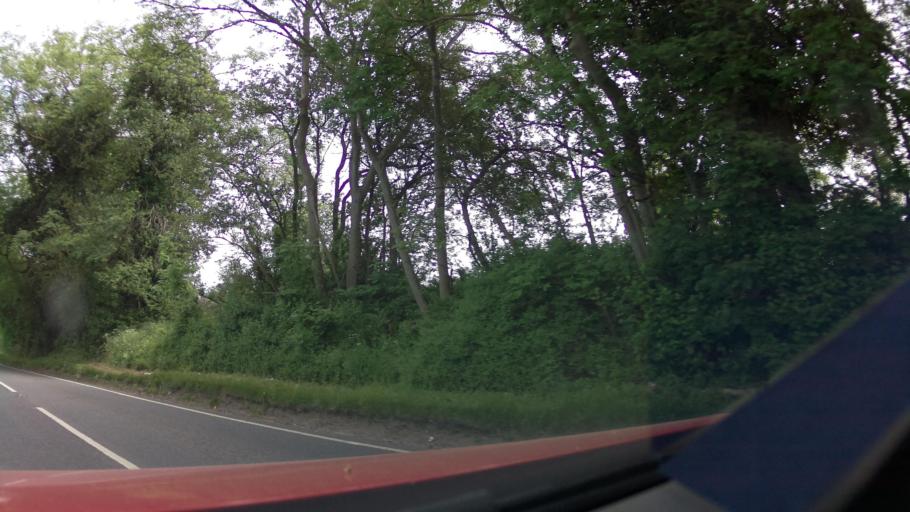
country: GB
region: England
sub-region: Worcestershire
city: Kempsey
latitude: 52.1621
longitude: -2.1613
